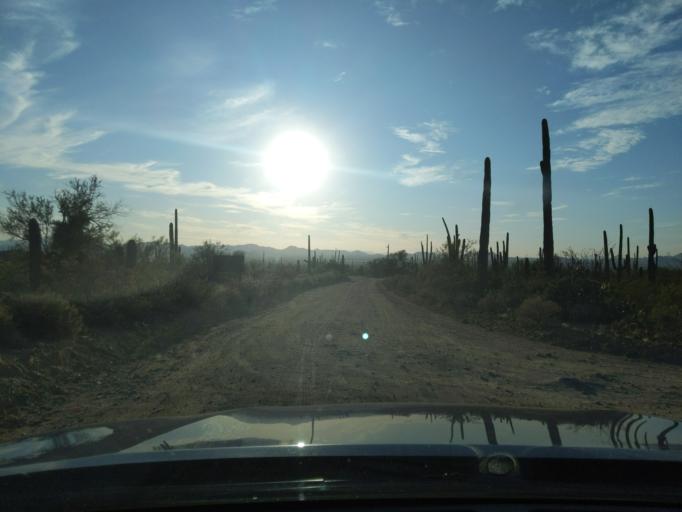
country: US
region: Arizona
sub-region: Pima County
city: Picture Rocks
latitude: 32.2873
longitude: -111.2026
